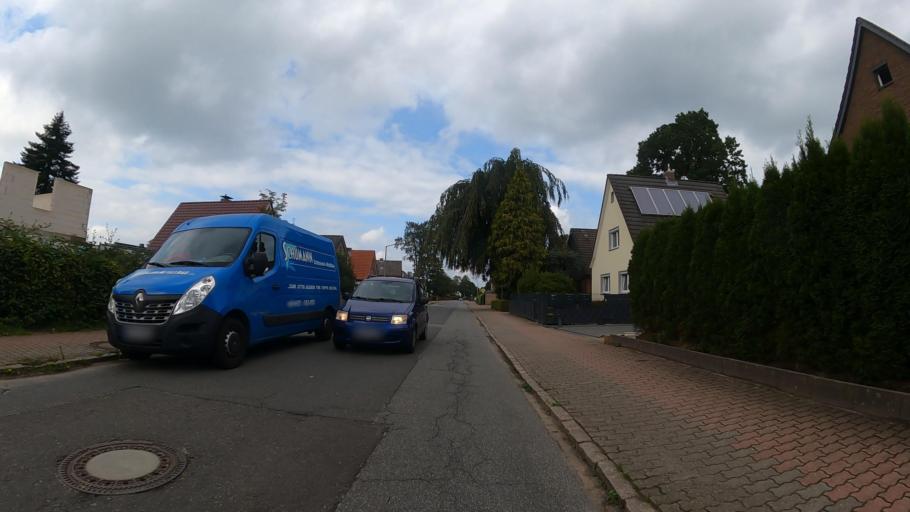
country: DE
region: Schleswig-Holstein
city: Tornesch
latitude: 53.7022
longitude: 9.7154
